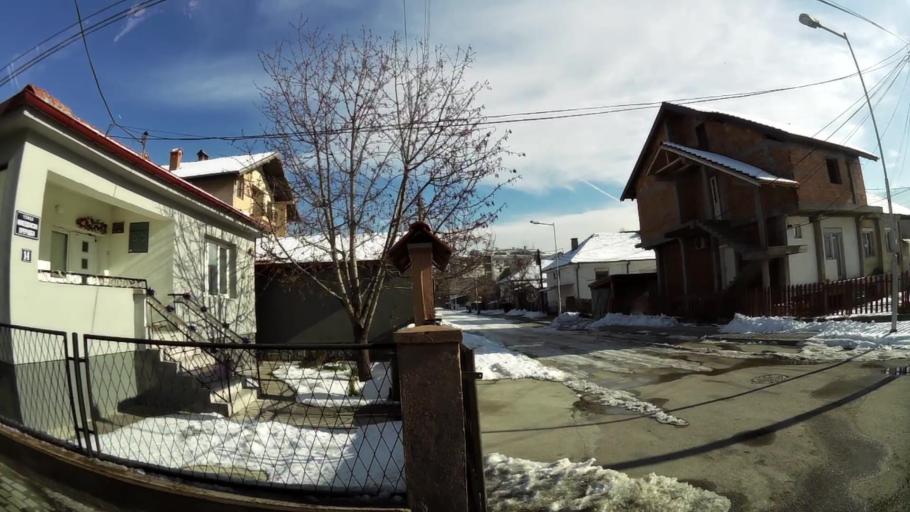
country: MK
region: Saraj
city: Saraj
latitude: 42.0098
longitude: 21.3575
